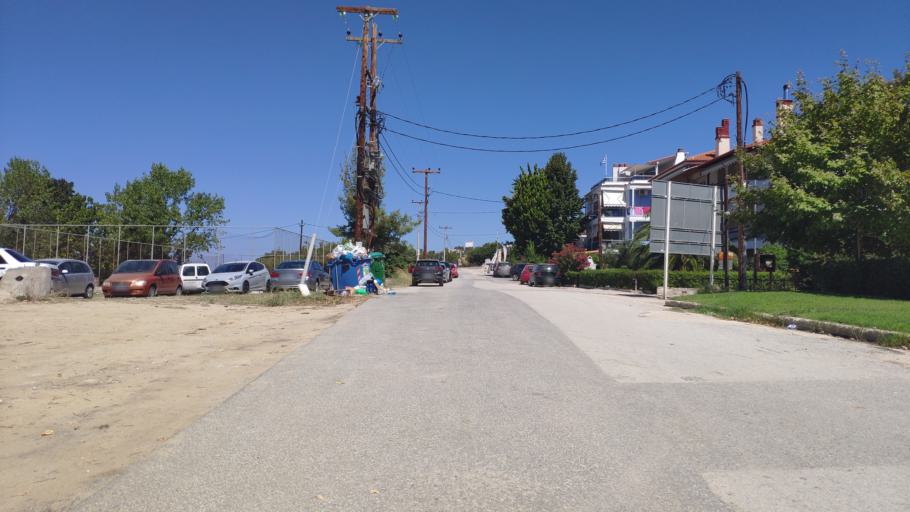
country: GR
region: Central Macedonia
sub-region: Nomos Chalkidikis
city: Kassandreia
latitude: 40.0338
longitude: 23.3618
